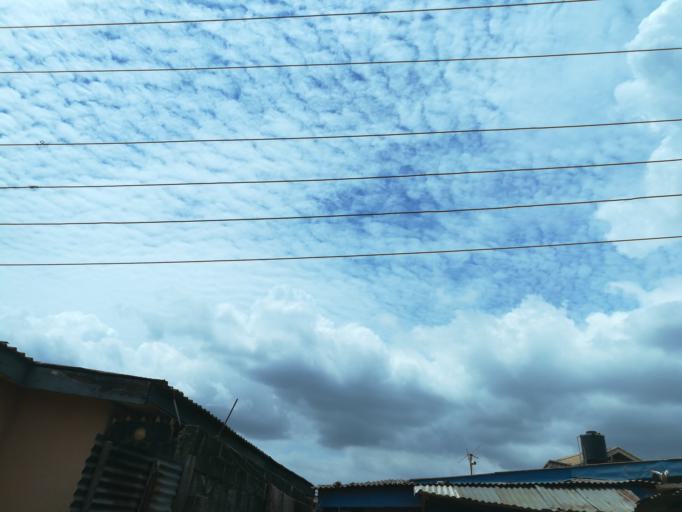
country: NG
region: Lagos
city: Oshodi
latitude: 6.5634
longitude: 3.3308
